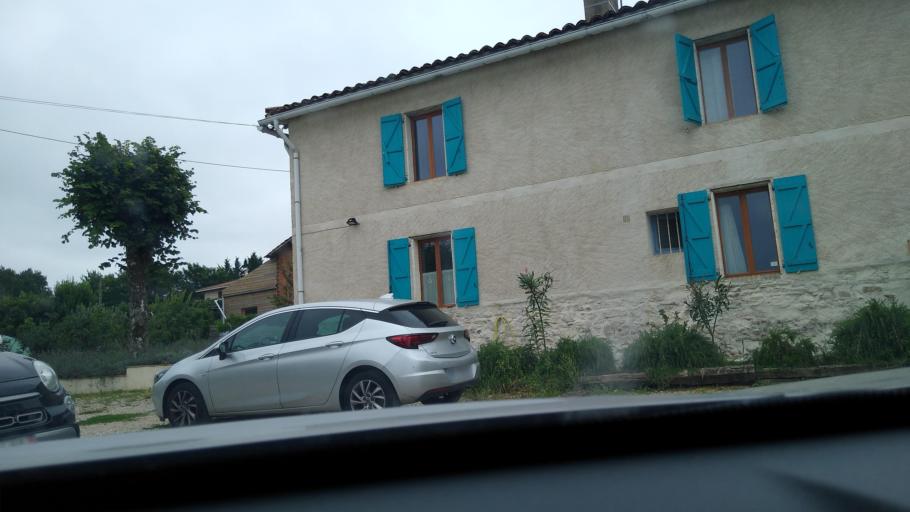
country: FR
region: Midi-Pyrenees
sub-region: Departement du Tarn
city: Brens
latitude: 43.8655
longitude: 1.9208
